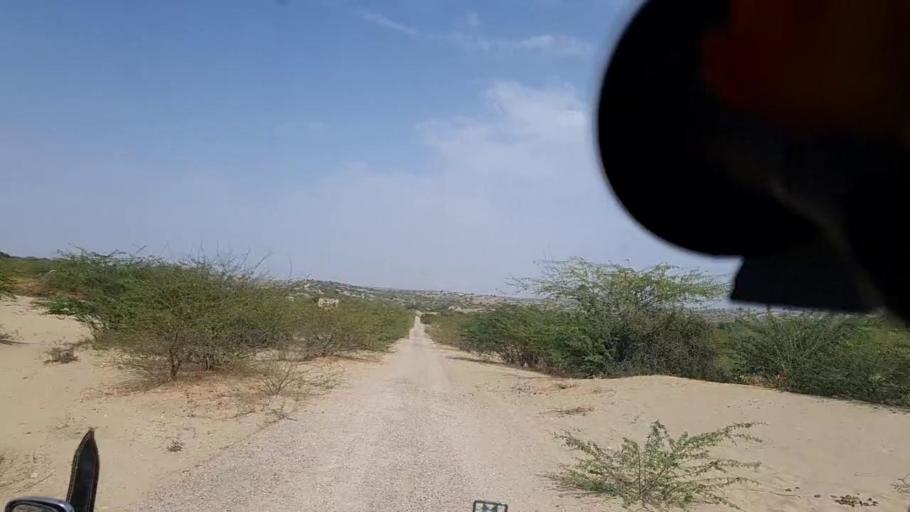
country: PK
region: Sindh
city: Diplo
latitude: 24.4328
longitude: 69.4303
